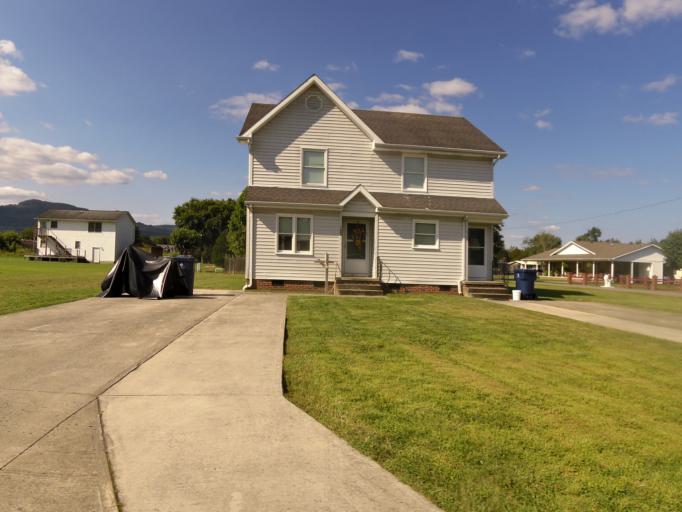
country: US
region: Kentucky
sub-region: Bell County
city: Middlesboro
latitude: 36.6008
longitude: -83.7281
